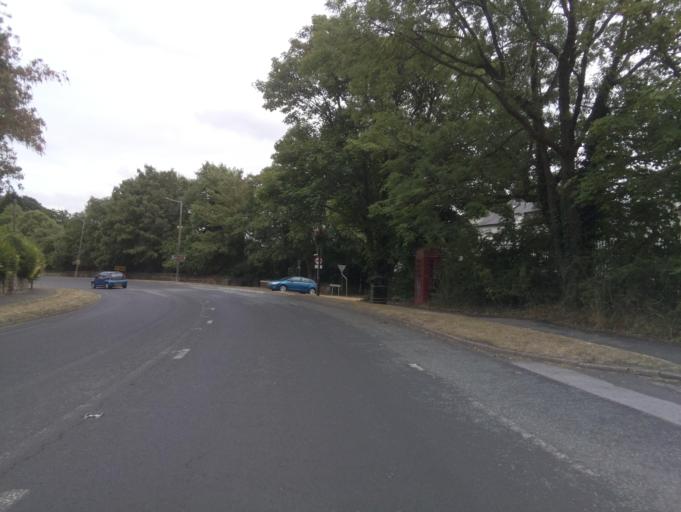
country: GB
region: England
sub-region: Derbyshire
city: Long Eaton
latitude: 52.9161
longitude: -1.3204
